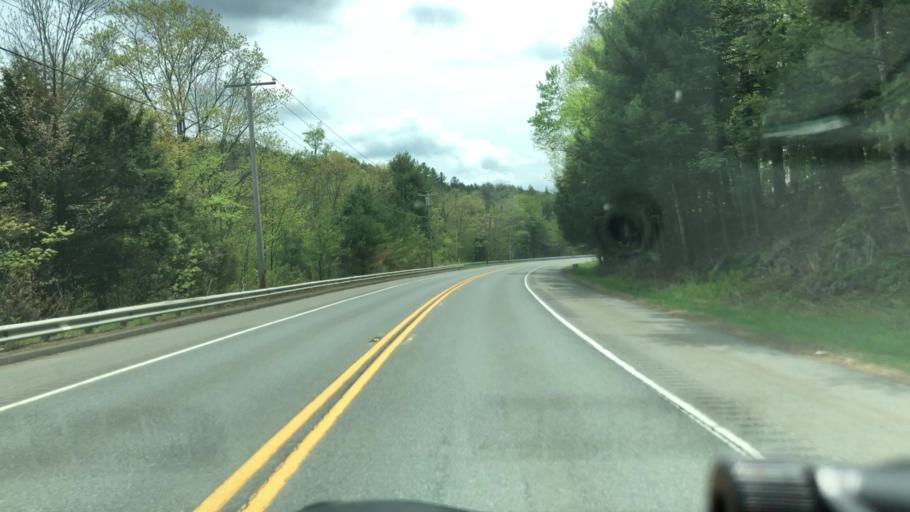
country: US
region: Massachusetts
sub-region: Hampshire County
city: Chesterfield
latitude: 42.4714
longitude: -72.9099
